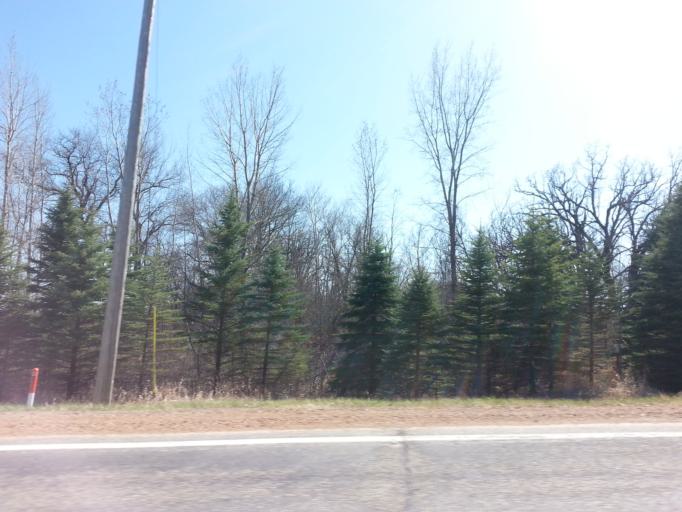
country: US
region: Minnesota
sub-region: Dakota County
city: Lakeville
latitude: 44.6523
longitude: -93.3205
